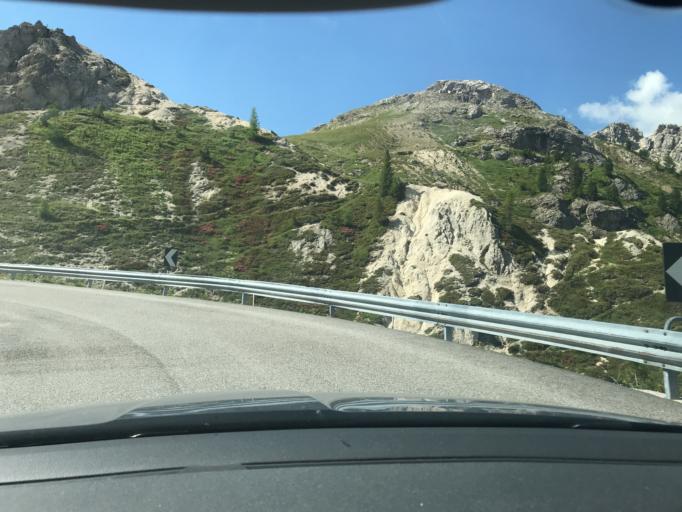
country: IT
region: Veneto
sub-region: Provincia di Belluno
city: Livinallongo del Col di Lana
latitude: 46.5335
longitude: 11.9862
